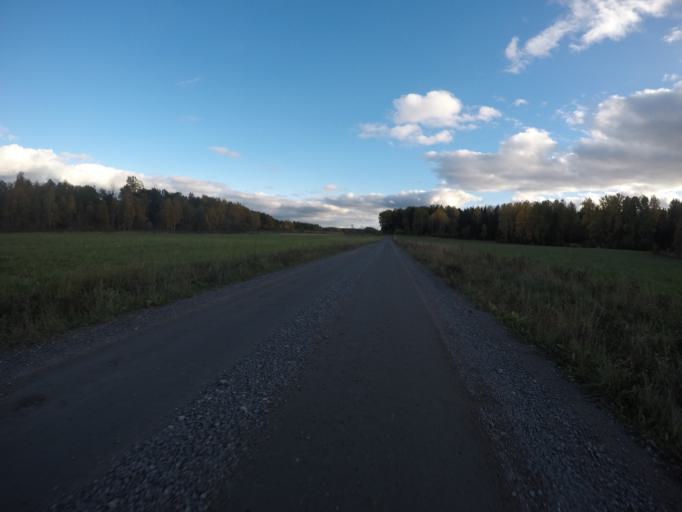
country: SE
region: Vaestmanland
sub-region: Arboga Kommun
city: Tyringe
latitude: 59.3102
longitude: 15.9752
